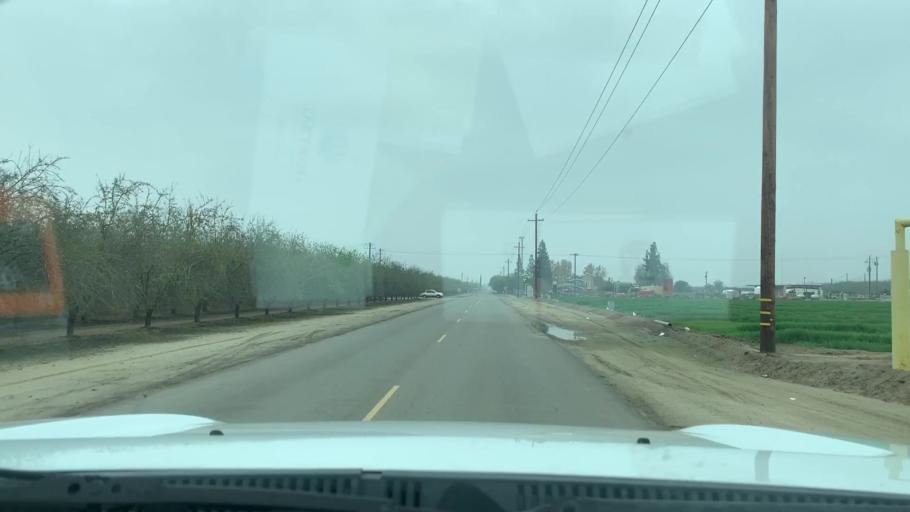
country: US
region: California
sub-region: Kern County
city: Shafter
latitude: 35.5086
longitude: -119.2960
